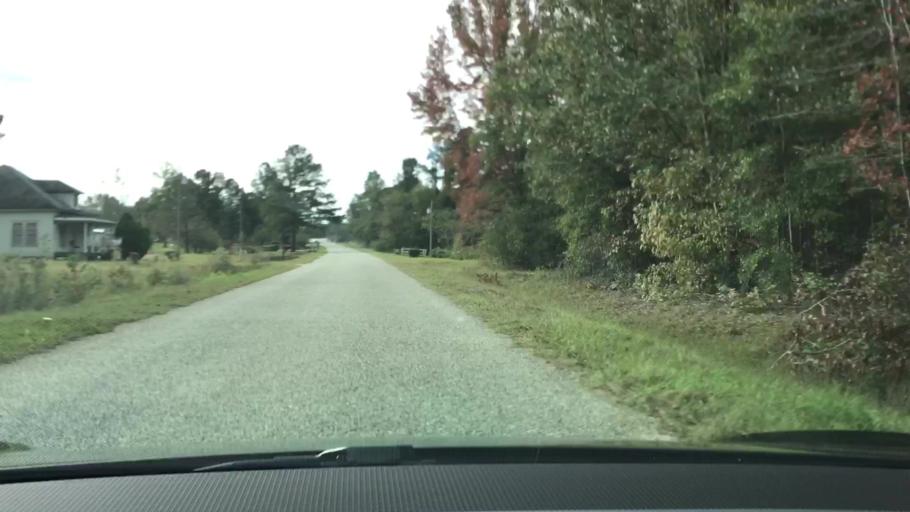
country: US
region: Georgia
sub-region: Jefferson County
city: Wadley
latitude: 32.8037
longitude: -82.3455
